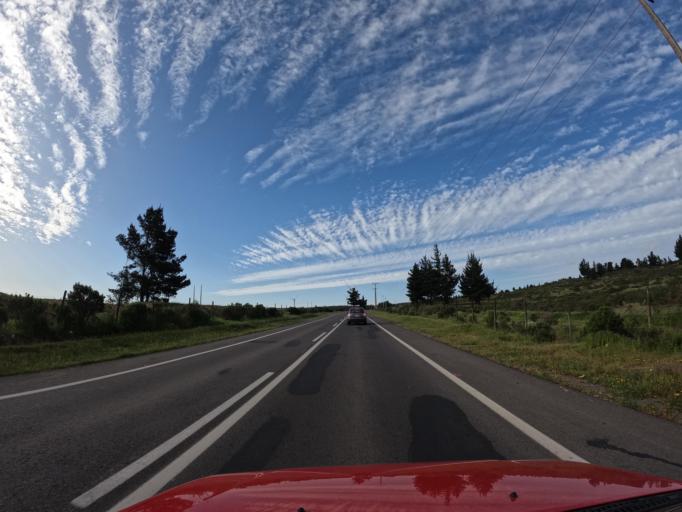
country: CL
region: Valparaiso
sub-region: San Antonio Province
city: San Antonio
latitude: -34.0581
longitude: -71.6257
